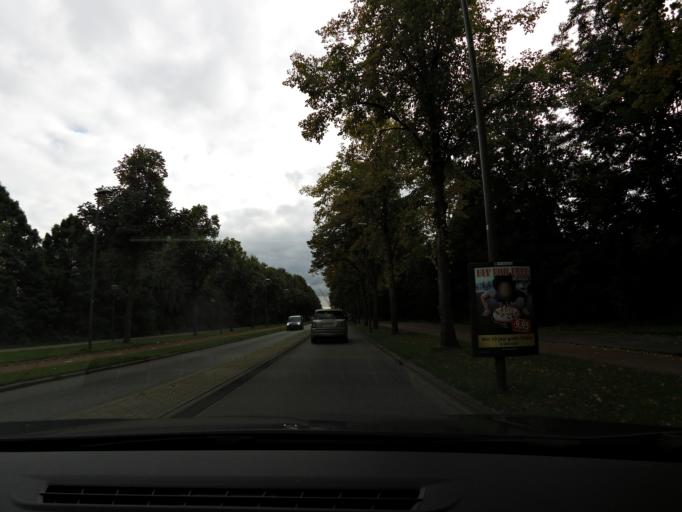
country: NL
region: South Holland
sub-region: Gemeente Schiedam
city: Schiedam
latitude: 51.9161
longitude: 4.3788
